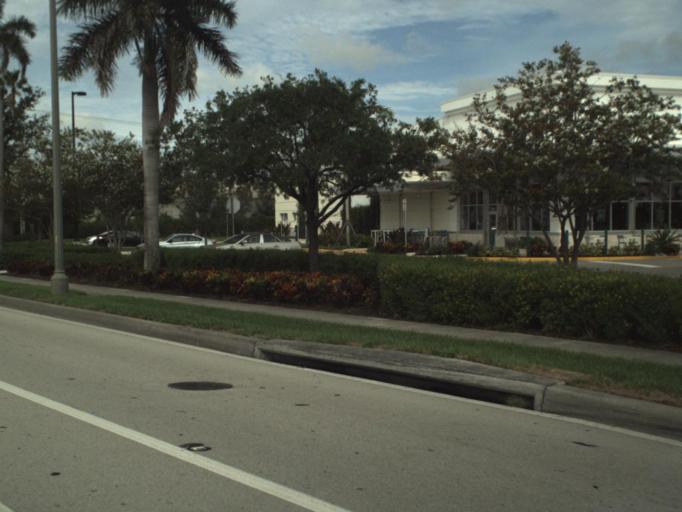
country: US
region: Florida
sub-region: Palm Beach County
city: Schall Circle
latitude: 26.7206
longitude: -80.0884
